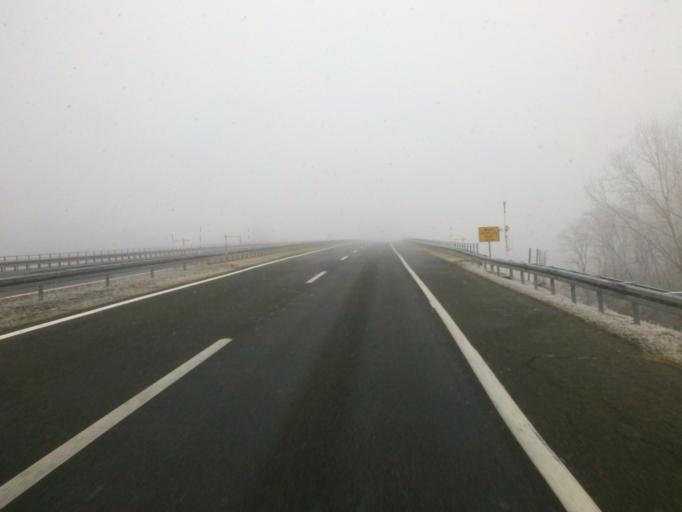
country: HR
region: Medimurska
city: Orehovica
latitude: 46.3117
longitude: 16.5080
